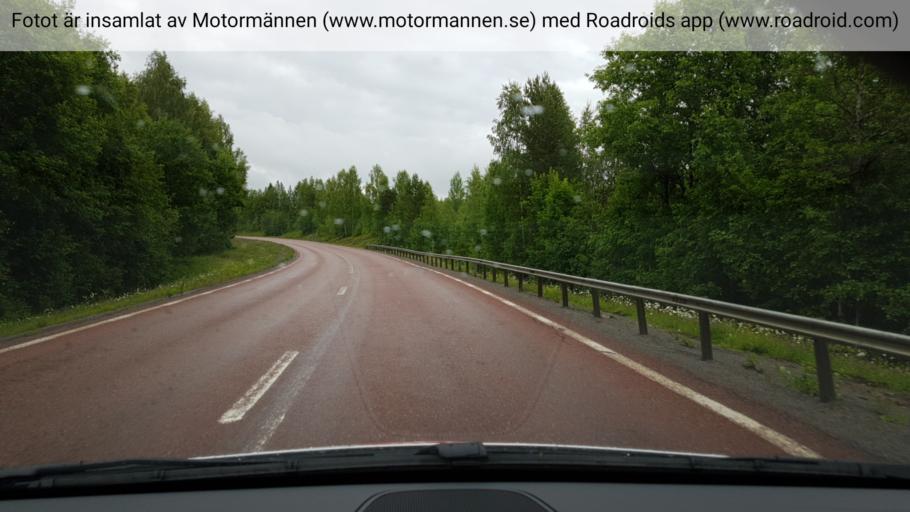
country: SE
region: Jaemtland
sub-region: Stroemsunds Kommun
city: Stroemsund
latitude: 64.0147
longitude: 15.9340
